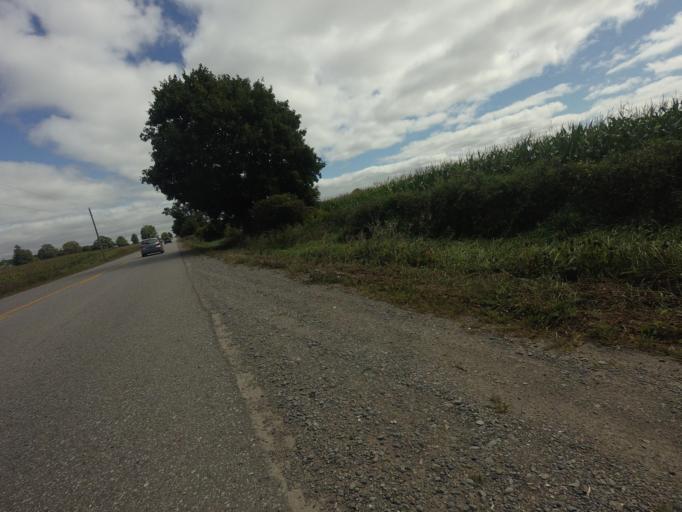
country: CA
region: Ontario
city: Uxbridge
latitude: 44.1138
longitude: -79.2194
